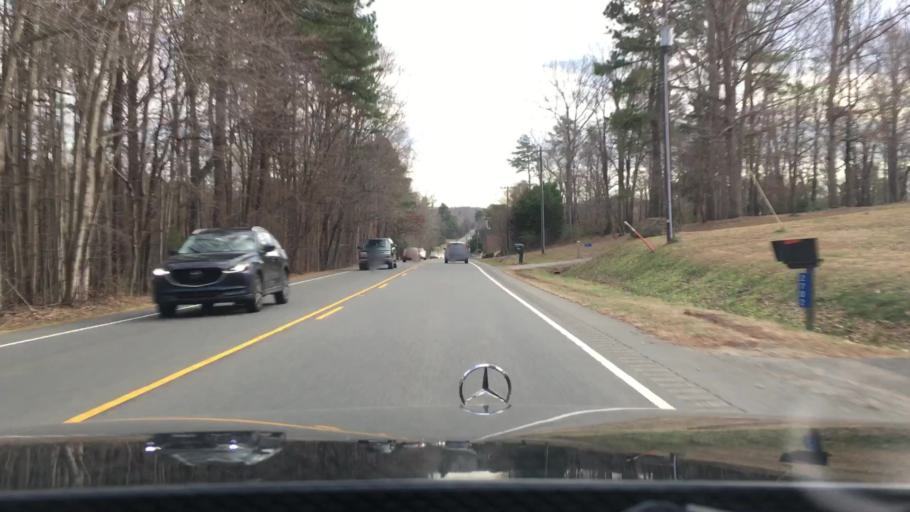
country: US
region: North Carolina
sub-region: Orange County
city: Hillsborough
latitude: 36.1284
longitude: -79.1178
